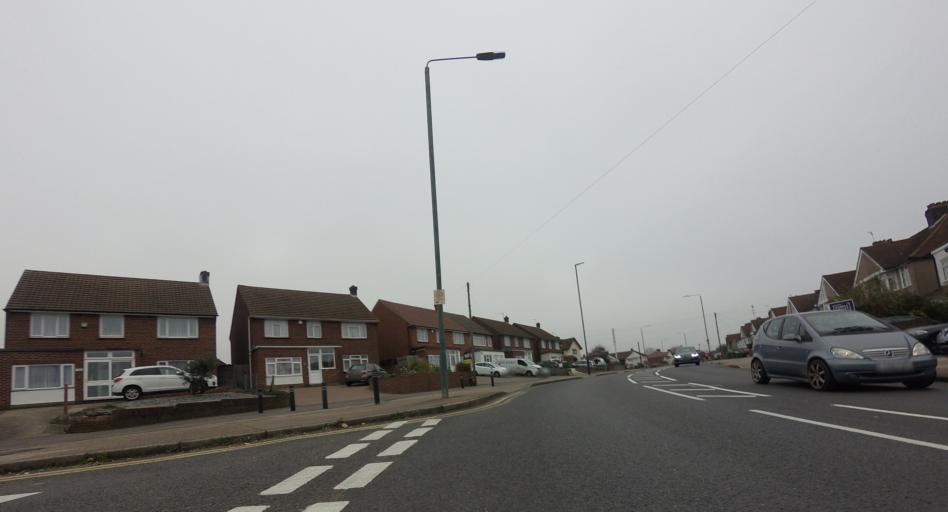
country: GB
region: England
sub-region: Greater London
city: Sidcup
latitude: 51.4414
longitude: 0.1174
